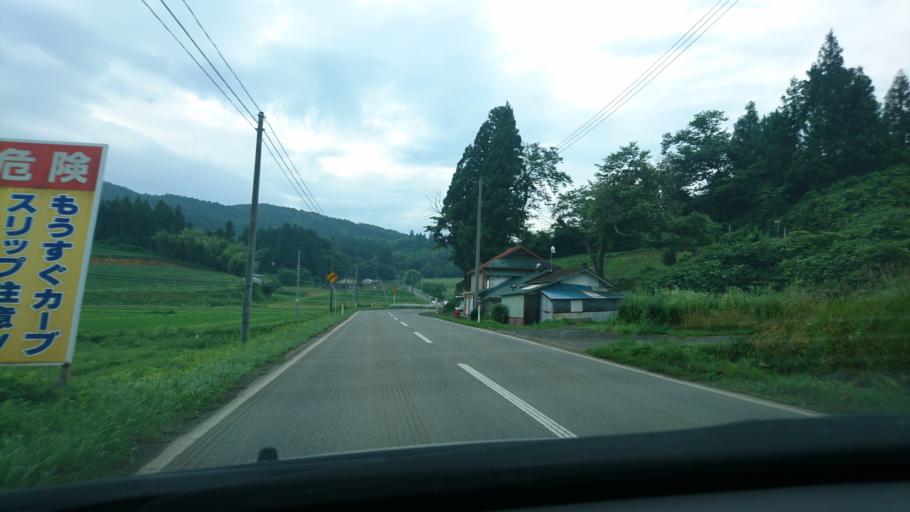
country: JP
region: Iwate
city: Ichinoseki
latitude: 38.9245
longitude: 141.4214
